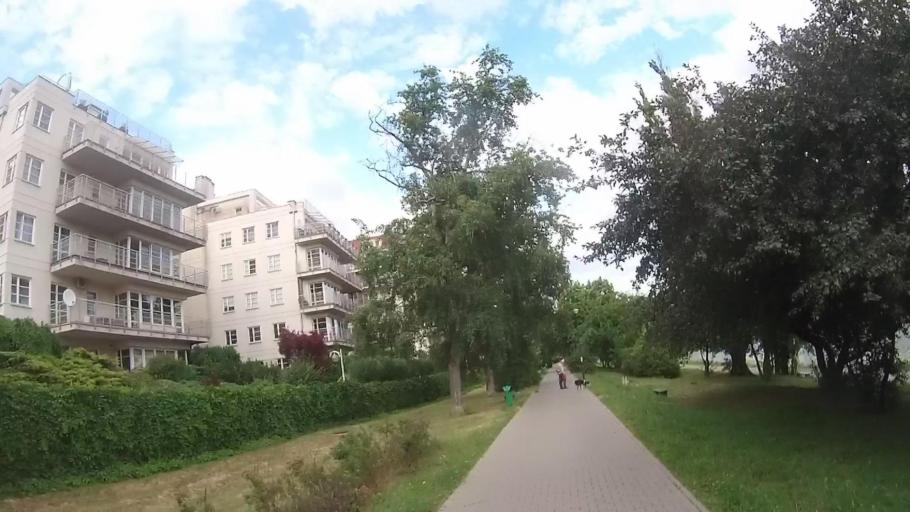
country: PL
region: Masovian Voivodeship
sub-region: Warszawa
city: Praga Polnoc
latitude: 52.2457
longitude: 21.0570
